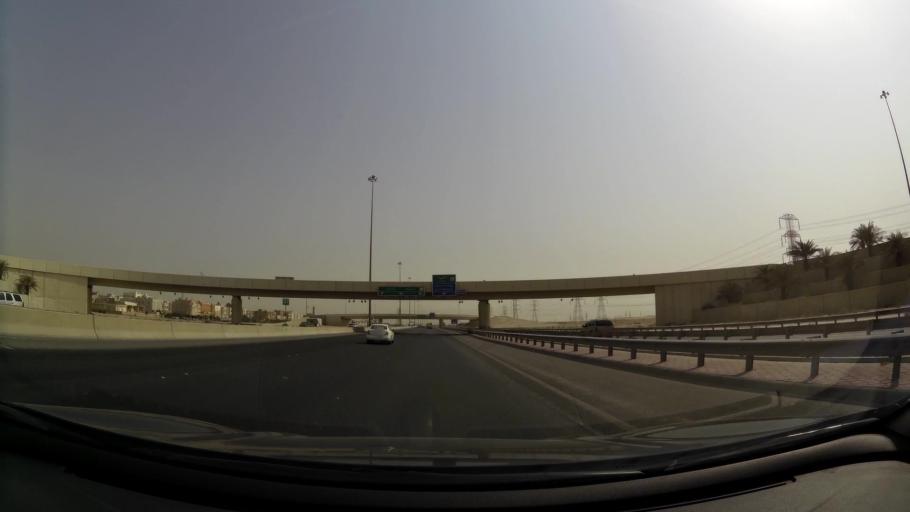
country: KW
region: Muhafazat al Jahra'
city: Al Jahra'
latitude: 29.2987
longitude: 47.7112
